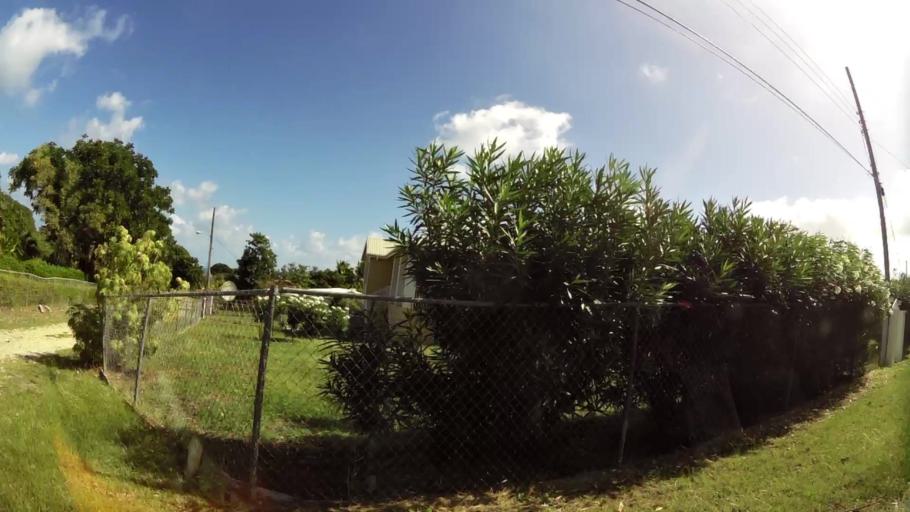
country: AG
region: Saint George
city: Piggotts
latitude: 17.1682
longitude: -61.8040
